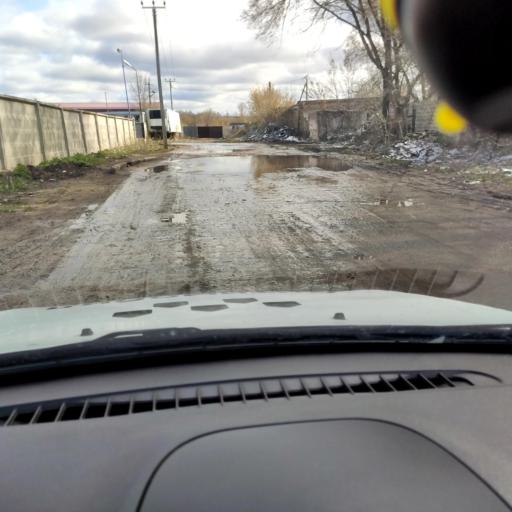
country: RU
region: Samara
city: Tol'yatti
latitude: 53.5606
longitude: 49.3182
